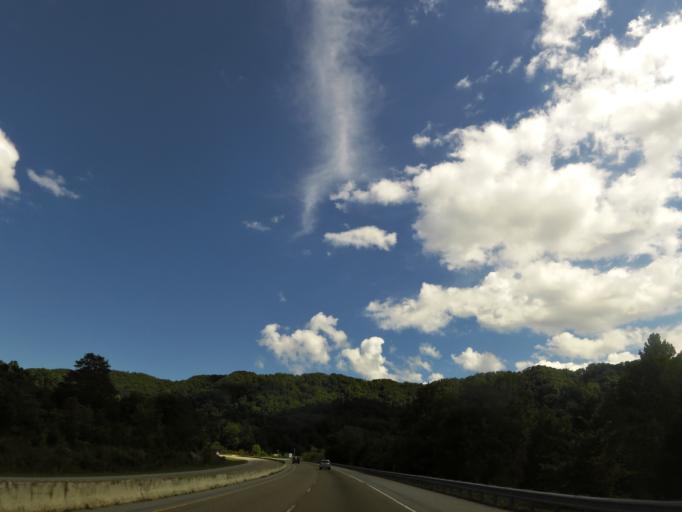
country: US
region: Tennessee
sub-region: Grainger County
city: Rutledge
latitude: 36.3501
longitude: -83.4337
